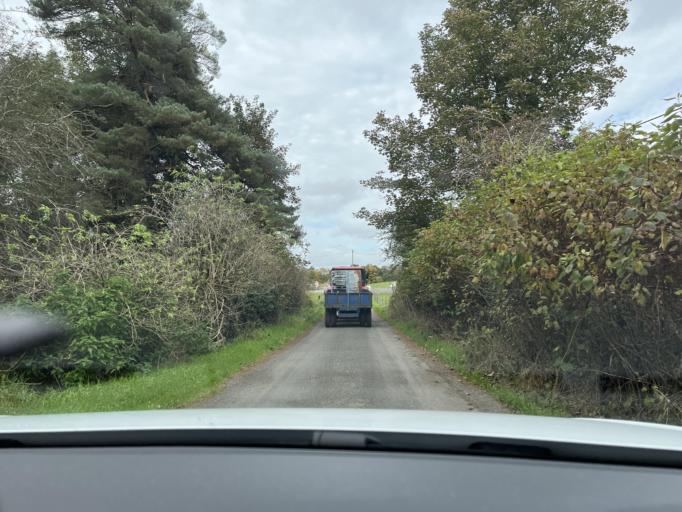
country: IE
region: Connaught
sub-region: Roscommon
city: Boyle
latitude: 53.9794
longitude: -8.2257
